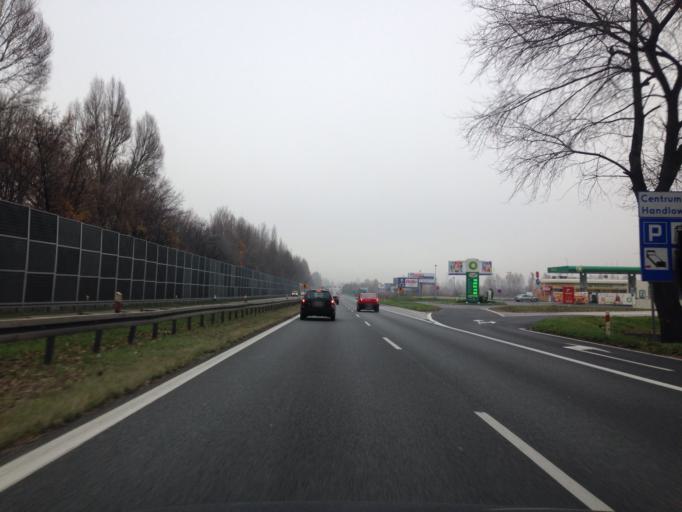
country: PL
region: Silesian Voivodeship
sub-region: Powiat bedzinski
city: Bedzin
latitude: 50.3183
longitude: 19.1085
